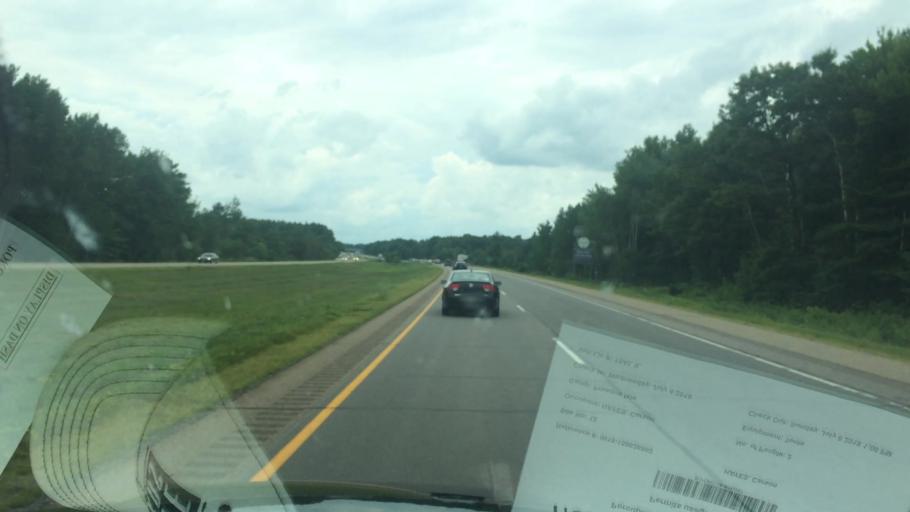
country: US
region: Wisconsin
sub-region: Marathon County
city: Mosinee
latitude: 44.7156
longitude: -89.6615
